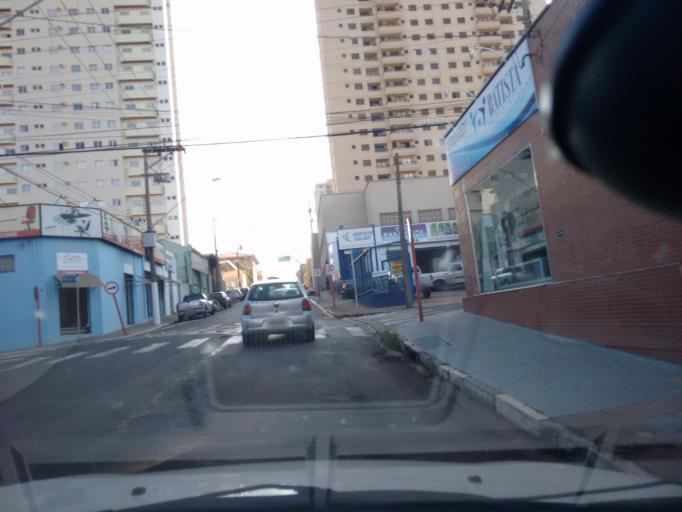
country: BR
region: Sao Paulo
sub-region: Araraquara
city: Araraquara
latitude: -21.7972
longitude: -48.1734
